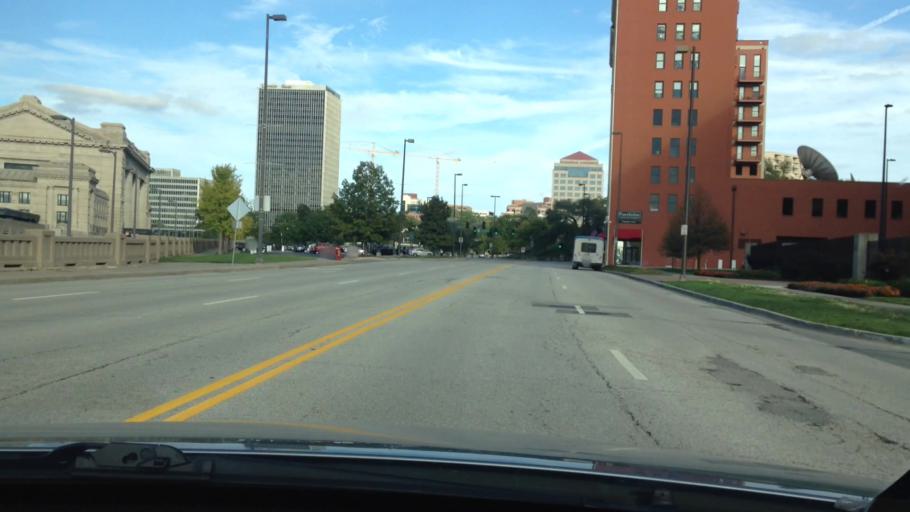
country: US
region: Missouri
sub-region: Jackson County
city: Kansas City
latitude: 39.0834
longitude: -94.5886
